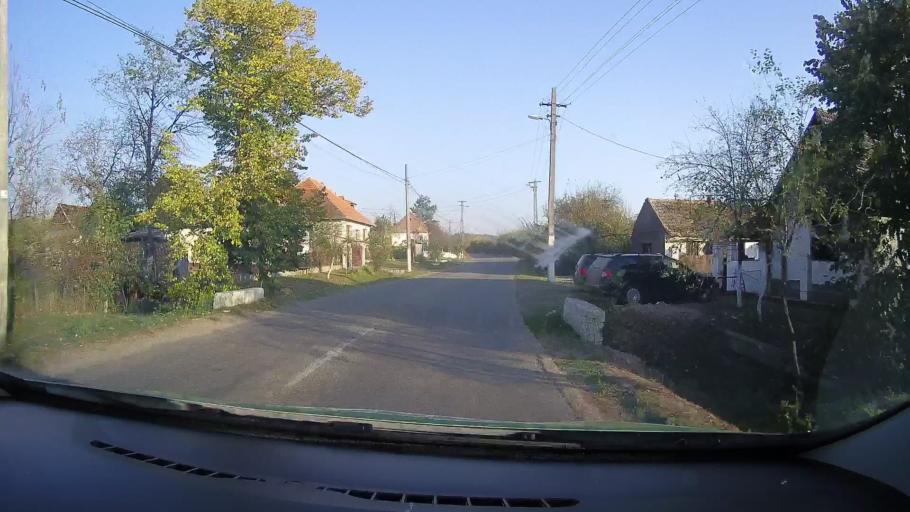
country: RO
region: Arad
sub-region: Comuna Silindia
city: Silindia
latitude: 46.3375
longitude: 21.9238
